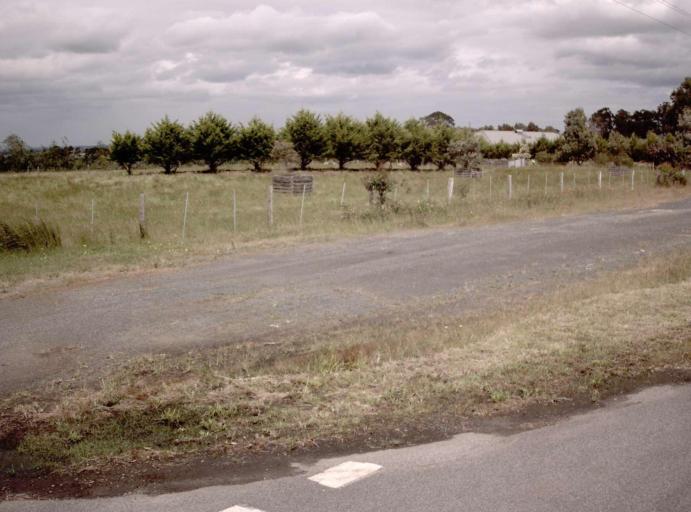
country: AU
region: Victoria
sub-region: Latrobe
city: Moe
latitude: -38.0794
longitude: 146.1882
